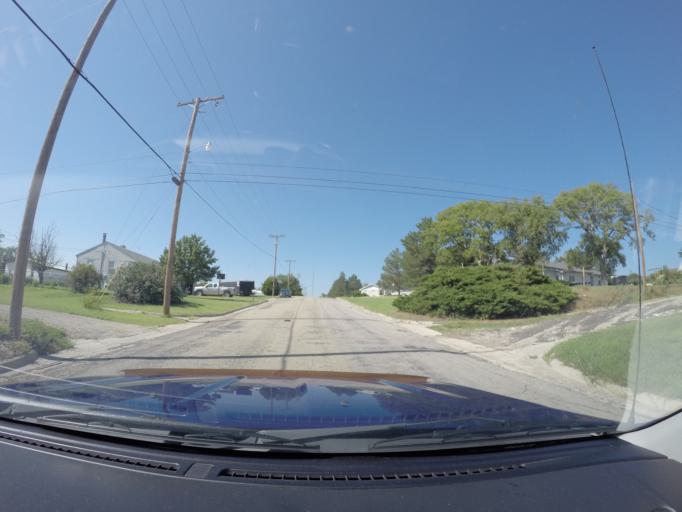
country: US
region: Kansas
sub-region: Rooks County
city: Stockton
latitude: 39.4417
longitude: -99.2722
